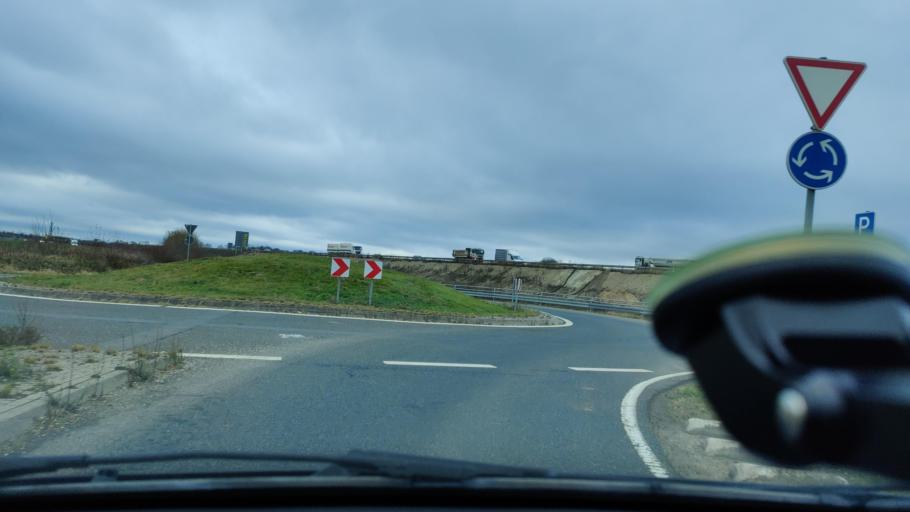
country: DE
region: North Rhine-Westphalia
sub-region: Regierungsbezirk Koln
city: Wurselen
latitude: 50.8242
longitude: 6.1786
